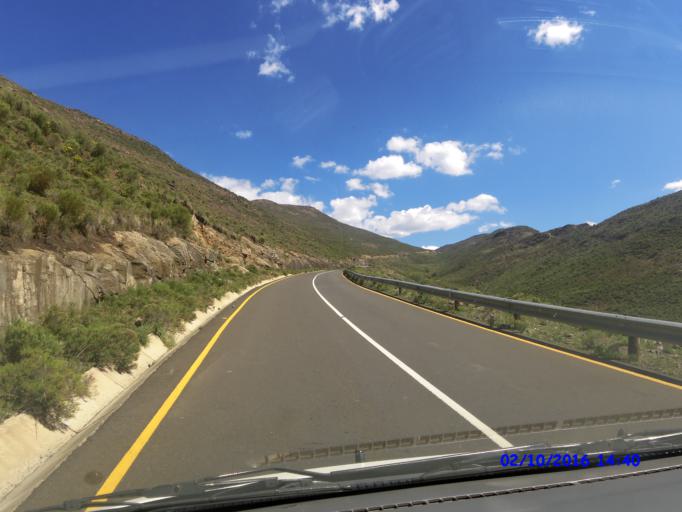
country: LS
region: Maseru
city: Nako
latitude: -29.5187
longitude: 28.0613
